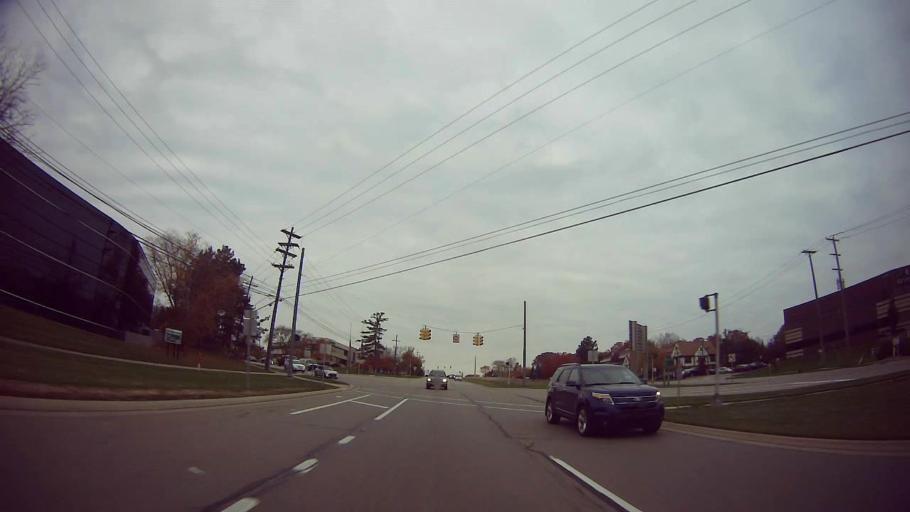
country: US
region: Michigan
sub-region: Oakland County
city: Franklin
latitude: 42.5142
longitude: -83.3324
